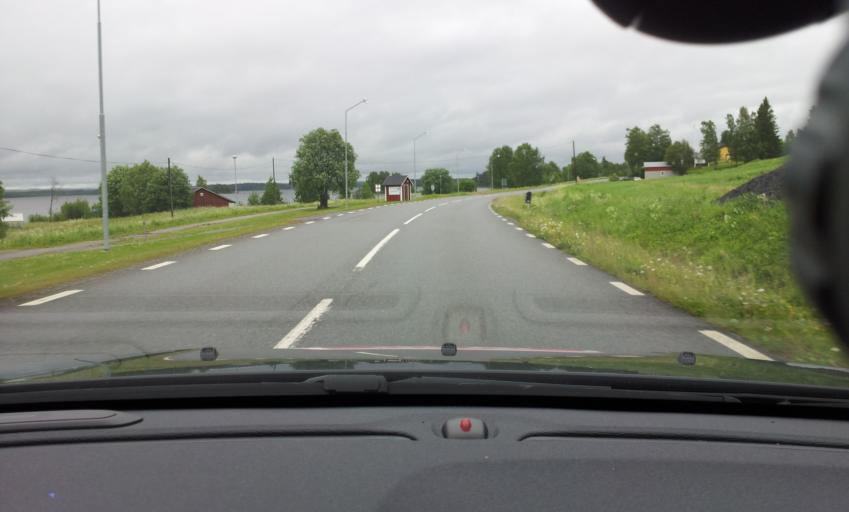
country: SE
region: Jaemtland
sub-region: Stroemsunds Kommun
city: Stroemsund
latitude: 63.5806
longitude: 15.3604
